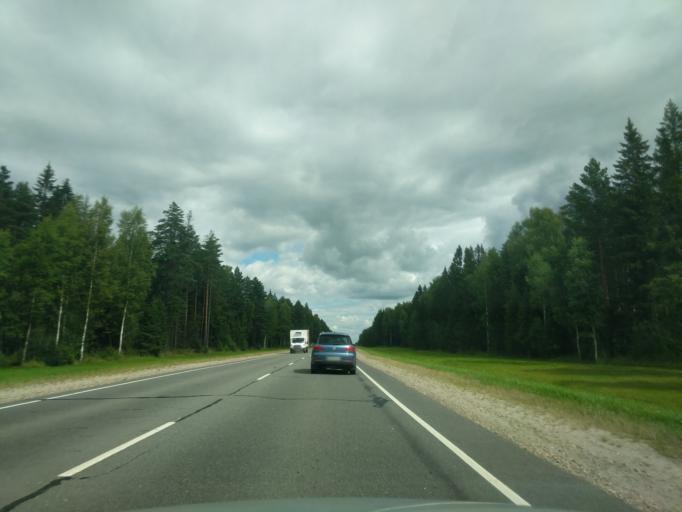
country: RU
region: Jaroslavl
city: Nekrasovskoye
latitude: 57.5995
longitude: 40.3146
